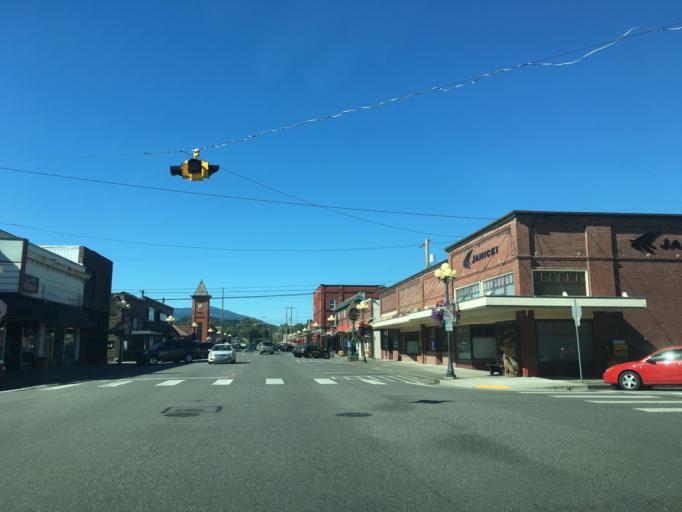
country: US
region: Washington
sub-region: Skagit County
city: Sedro-Woolley
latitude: 48.5045
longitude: -122.2386
